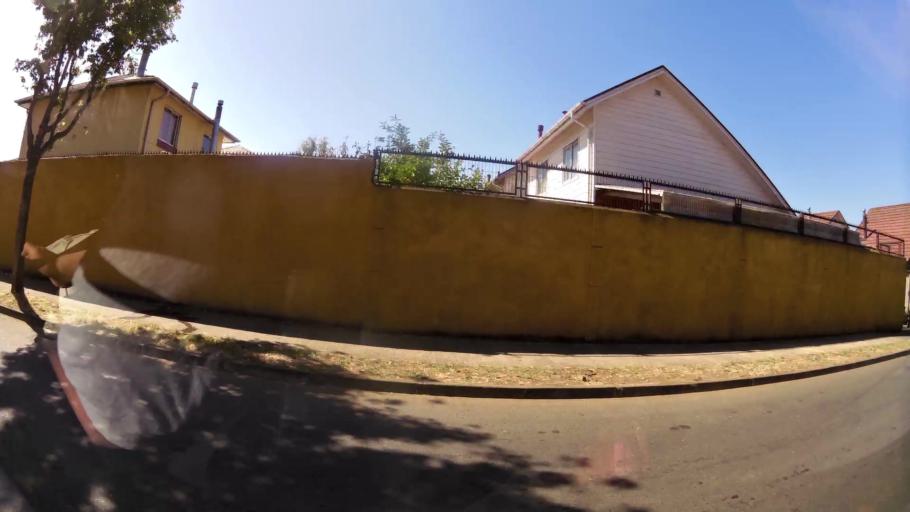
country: CL
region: Biobio
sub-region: Provincia de Concepcion
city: Concepcion
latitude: -36.7856
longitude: -73.0395
